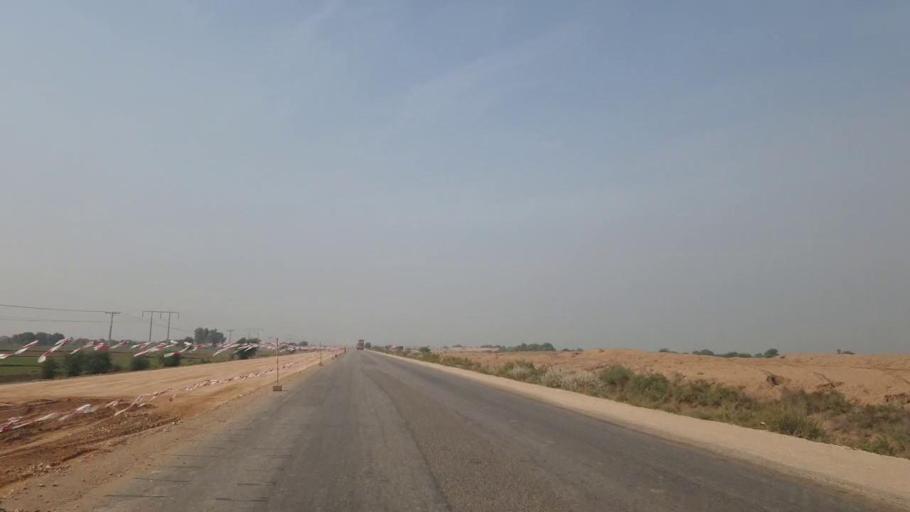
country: PK
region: Sindh
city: Sann
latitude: 26.1372
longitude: 68.0423
